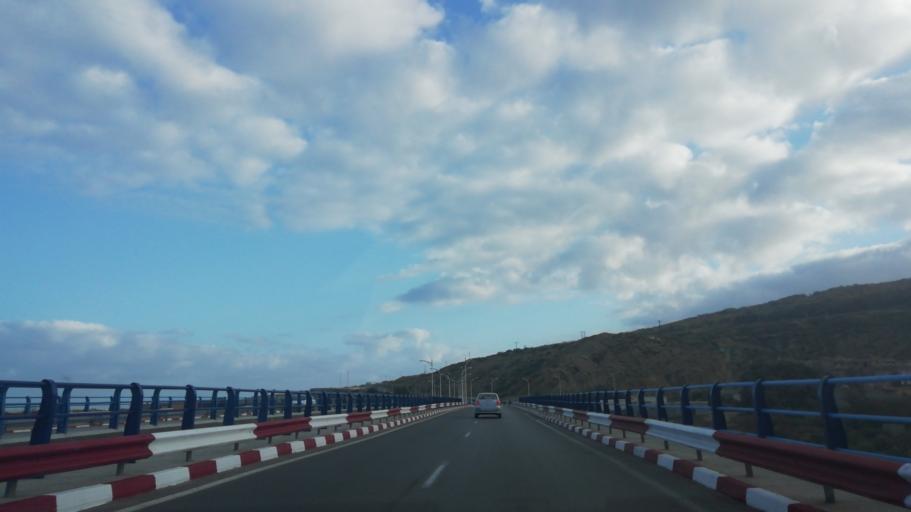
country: DZ
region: Mostaganem
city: Mostaganem
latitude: 36.0342
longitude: 0.1411
